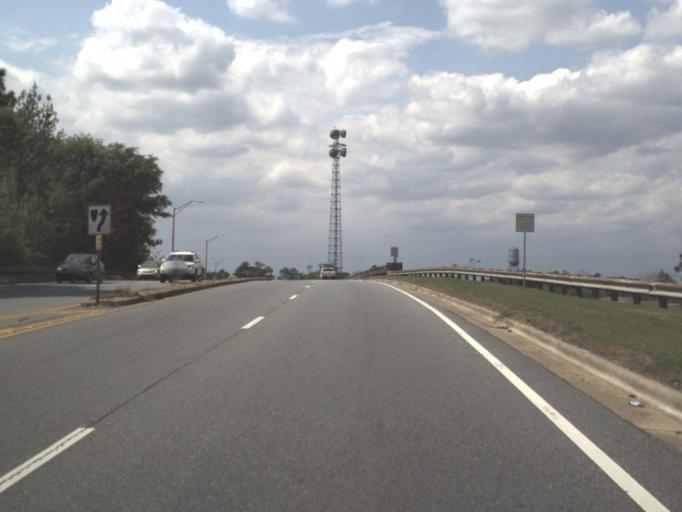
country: US
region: Alabama
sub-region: Escambia County
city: Flomaton
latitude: 30.9982
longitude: -87.2606
